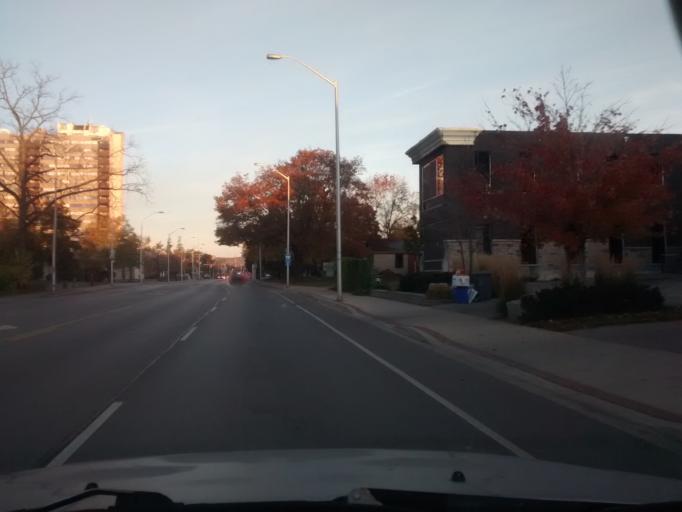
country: CA
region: Ontario
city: Burlington
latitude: 43.3315
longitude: -79.8062
